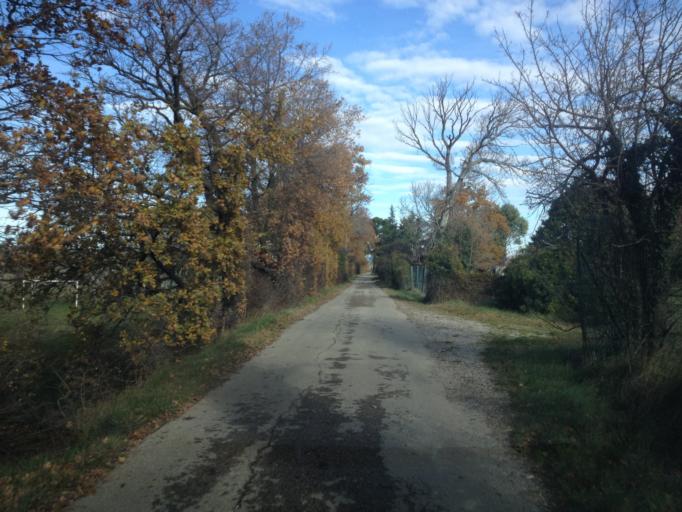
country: FR
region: Provence-Alpes-Cote d'Azur
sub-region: Departement du Vaucluse
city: Jonquieres
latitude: 44.0890
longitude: 4.9197
